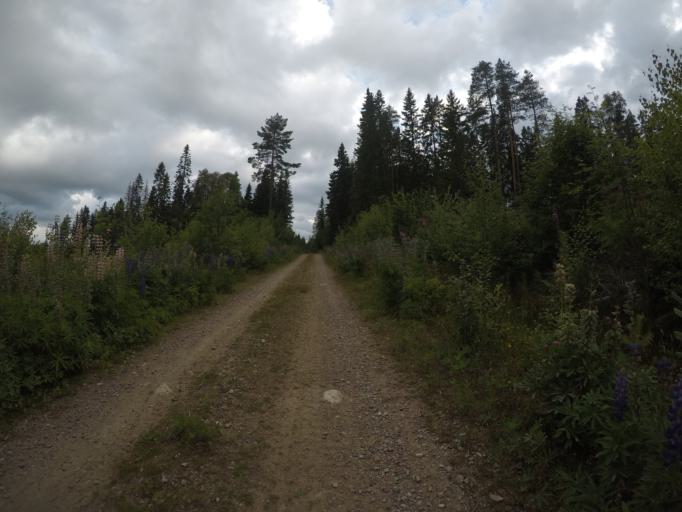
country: SE
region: Vaermland
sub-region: Filipstads Kommun
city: Lesjofors
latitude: 60.1493
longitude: 14.3917
